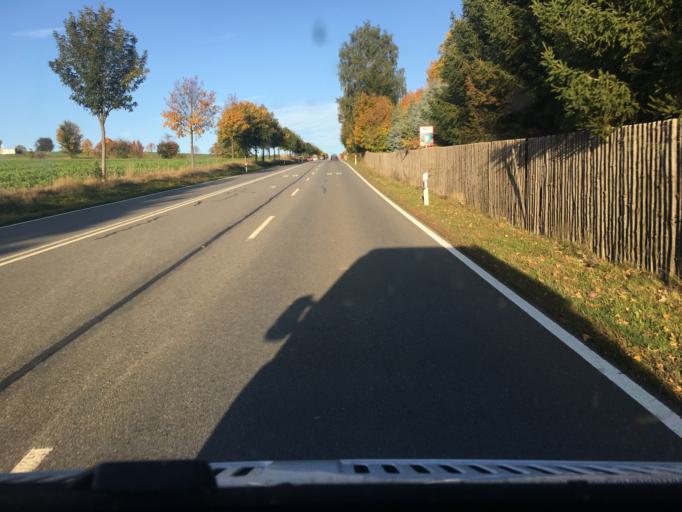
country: DE
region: Saxony
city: Schneeberg
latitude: 50.5990
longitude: 12.6266
